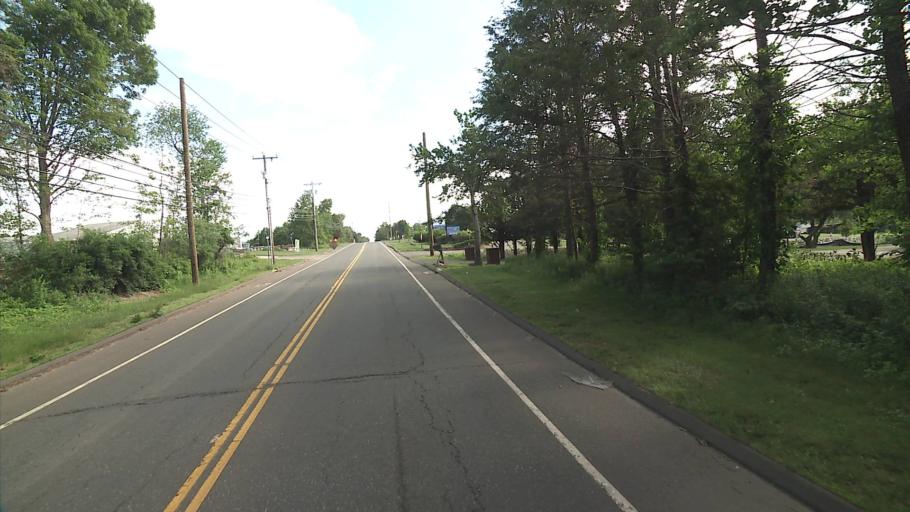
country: US
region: Connecticut
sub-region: New Haven County
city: Prospect
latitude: 41.4349
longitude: -72.9926
